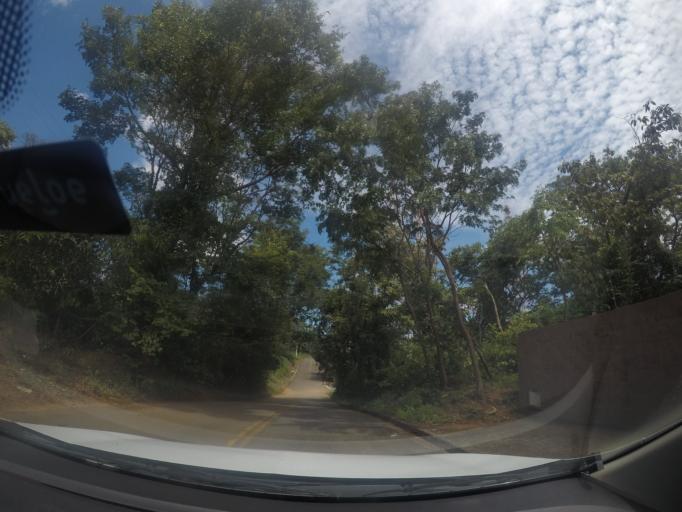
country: BR
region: Goias
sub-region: Goiania
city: Goiania
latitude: -16.6645
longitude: -49.3409
